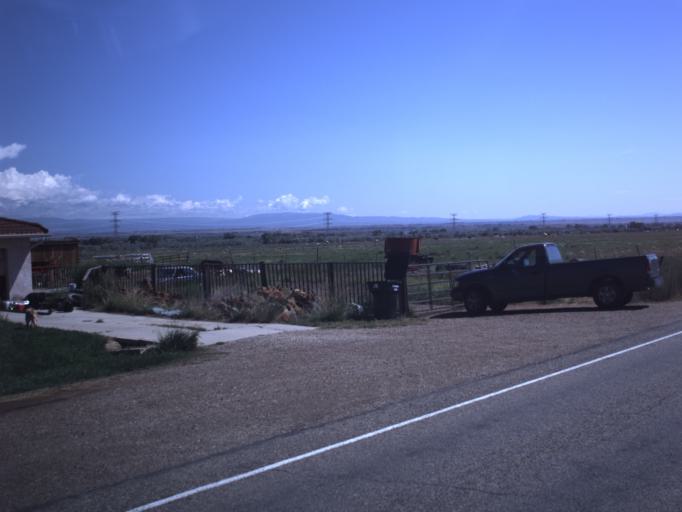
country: US
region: Utah
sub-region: Duchesne County
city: Roosevelt
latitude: 40.2584
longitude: -110.1023
